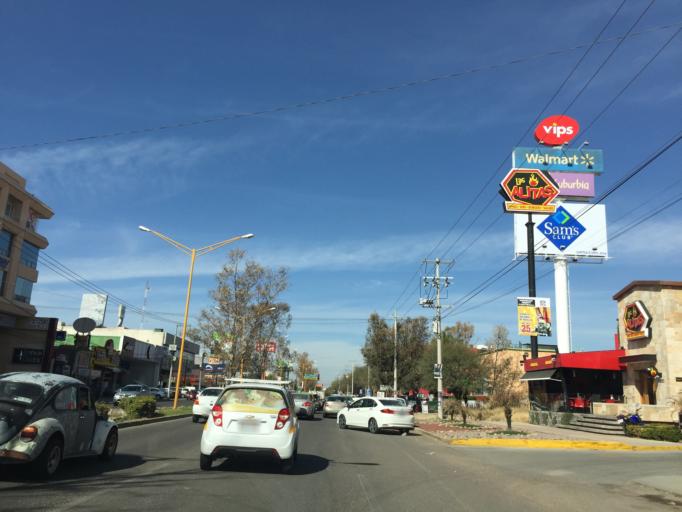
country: MX
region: Aguascalientes
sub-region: Jesus Maria
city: El Llano
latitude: 21.9218
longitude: -102.2978
